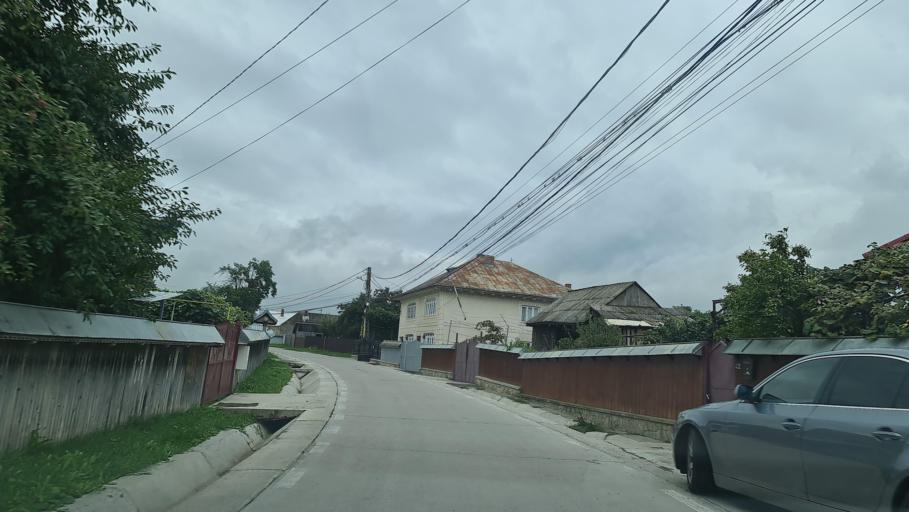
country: RO
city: Vanatori-Neamt
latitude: 47.2094
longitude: 26.3213
